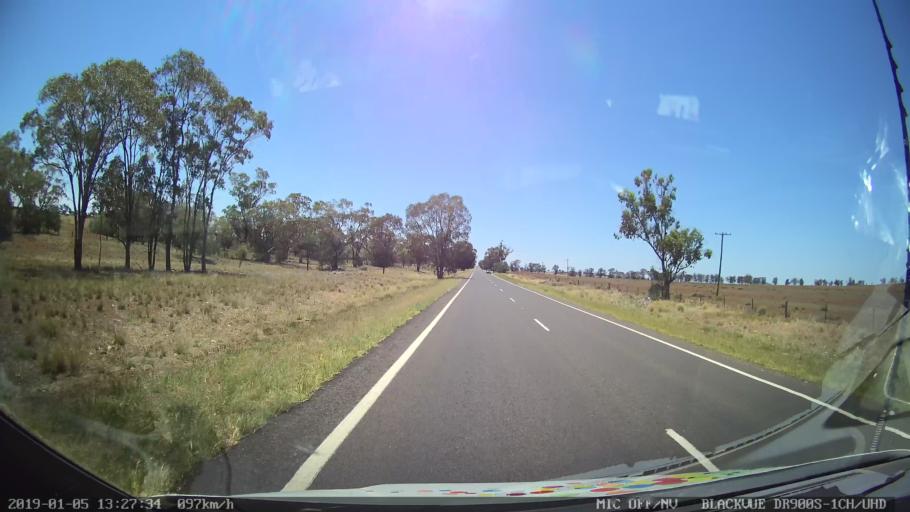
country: AU
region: New South Wales
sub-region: Gunnedah
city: Gunnedah
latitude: -31.0434
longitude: 150.0312
